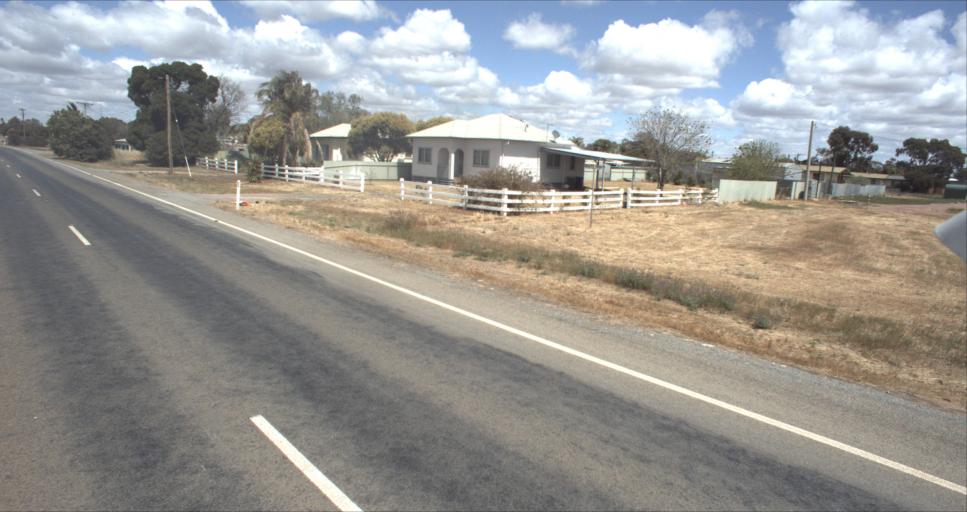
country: AU
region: New South Wales
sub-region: Murrumbidgee Shire
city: Darlington Point
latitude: -34.5143
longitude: 146.1857
